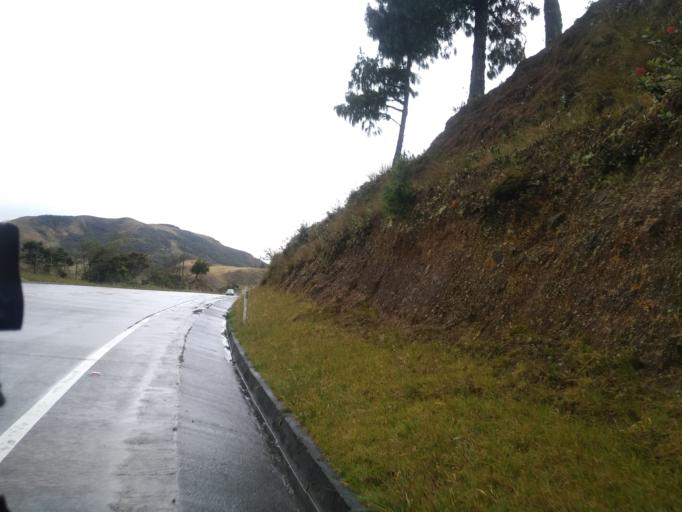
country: EC
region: Loja
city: Loja
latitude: -3.8941
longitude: -79.2614
